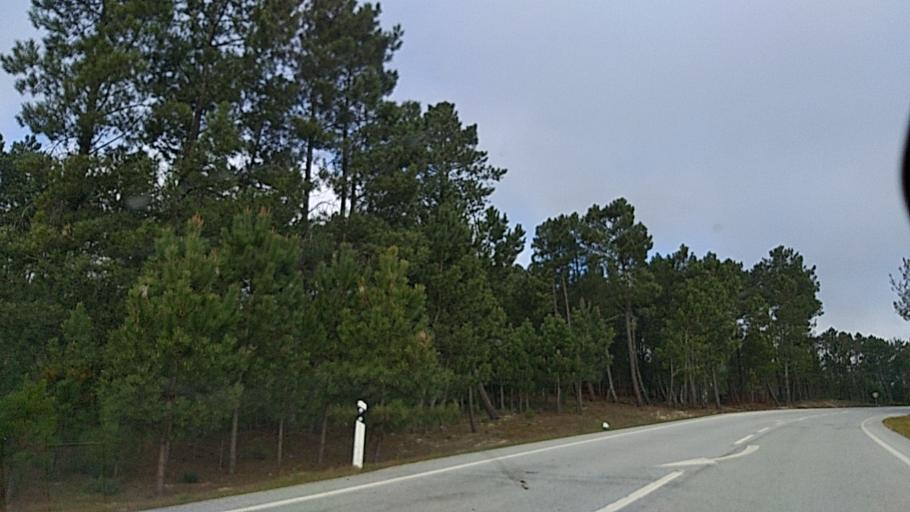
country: PT
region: Guarda
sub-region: Aguiar da Beira
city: Aguiar da Beira
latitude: 40.7495
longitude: -7.5046
